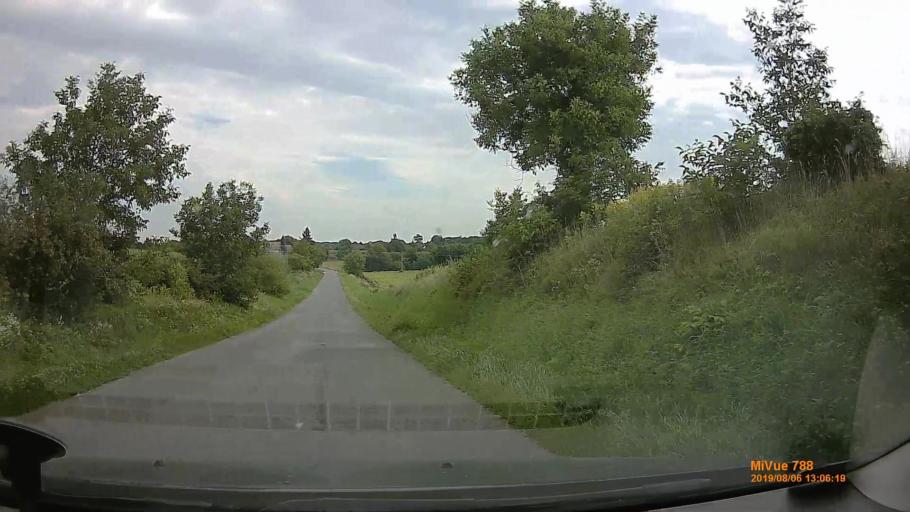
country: HU
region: Zala
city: Pacsa
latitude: 46.6306
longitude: 17.0507
